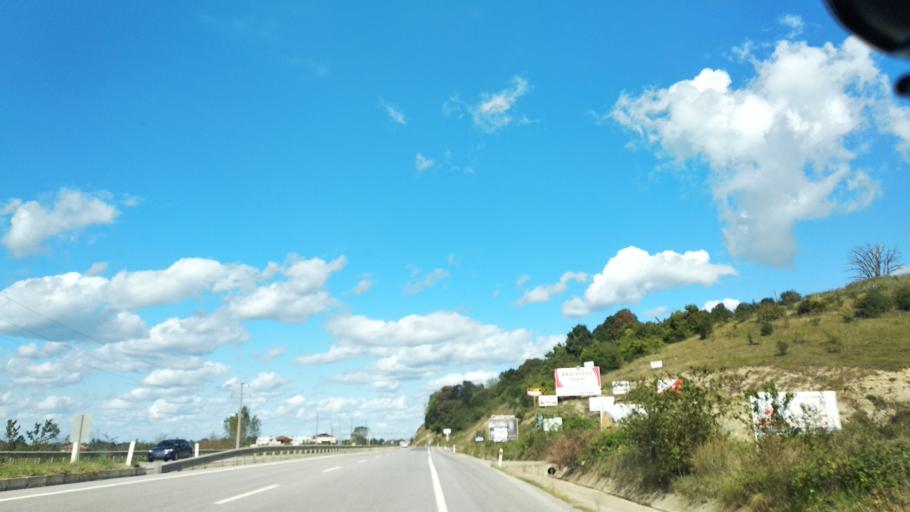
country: TR
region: Sakarya
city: Karasu
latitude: 41.0967
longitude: 30.6543
